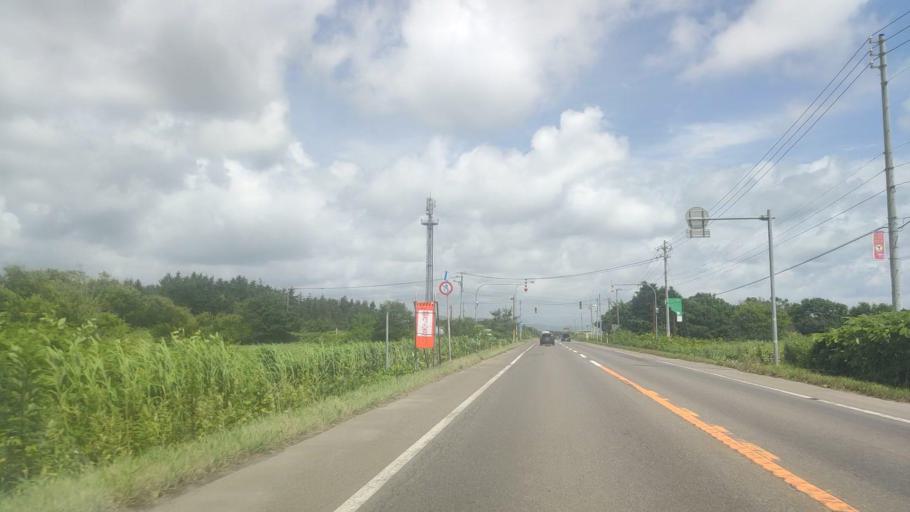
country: JP
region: Hokkaido
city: Niseko Town
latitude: 42.4804
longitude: 140.3500
